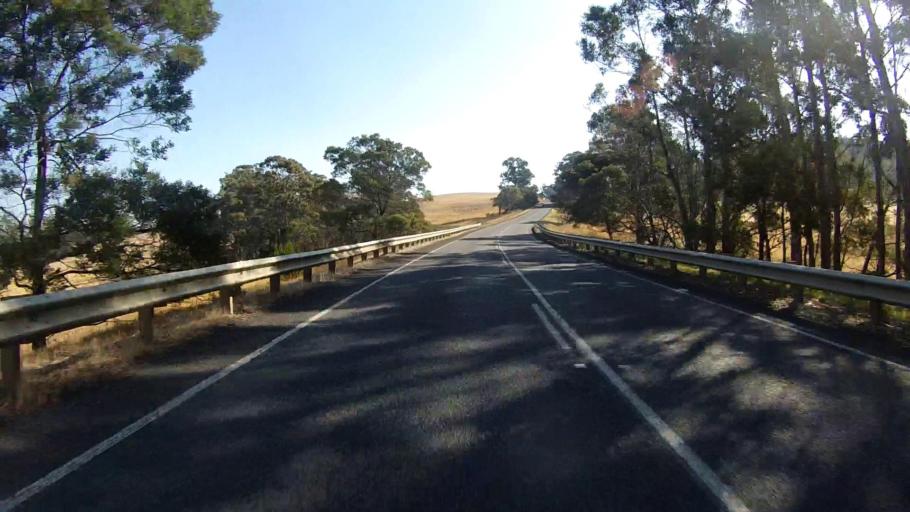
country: AU
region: Tasmania
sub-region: Sorell
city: Sorell
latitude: -42.7028
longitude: 147.5206
